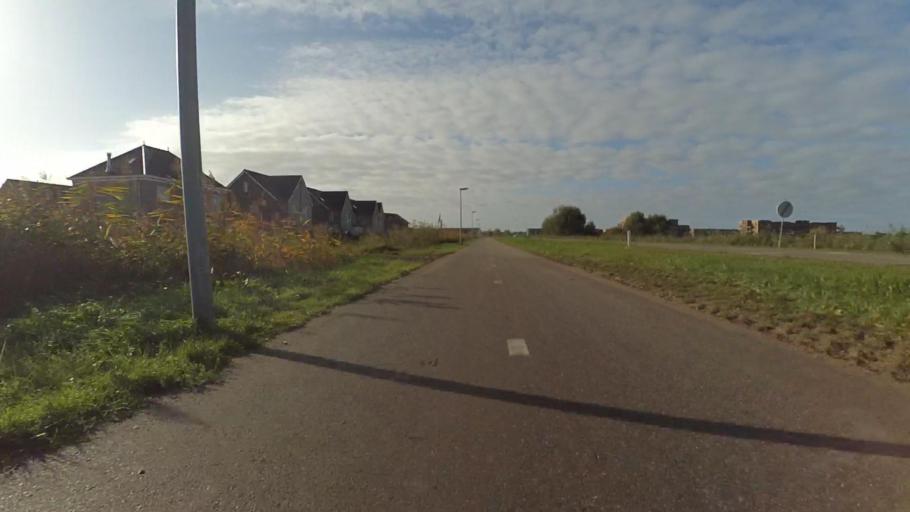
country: NL
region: Flevoland
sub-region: Gemeente Zeewolde
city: Zeewolde
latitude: 52.3456
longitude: 5.5320
